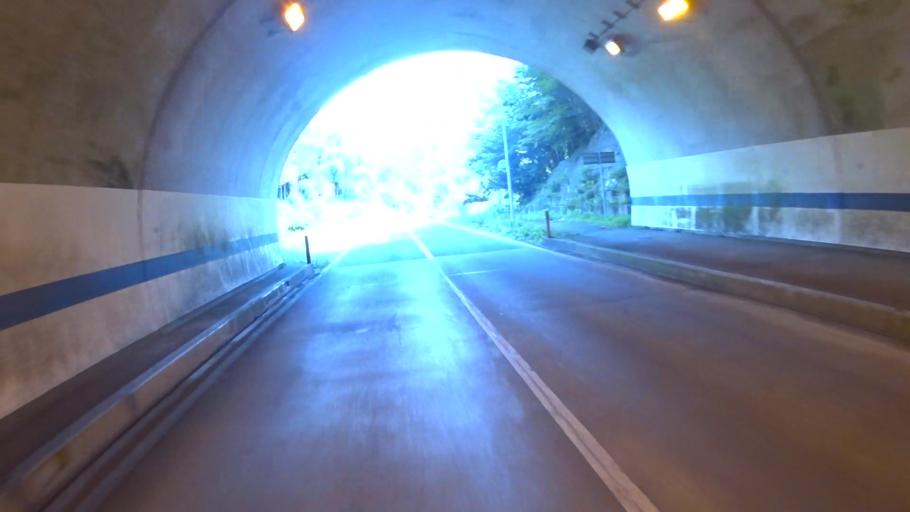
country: JP
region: Kyoto
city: Miyazu
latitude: 35.6635
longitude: 135.2605
